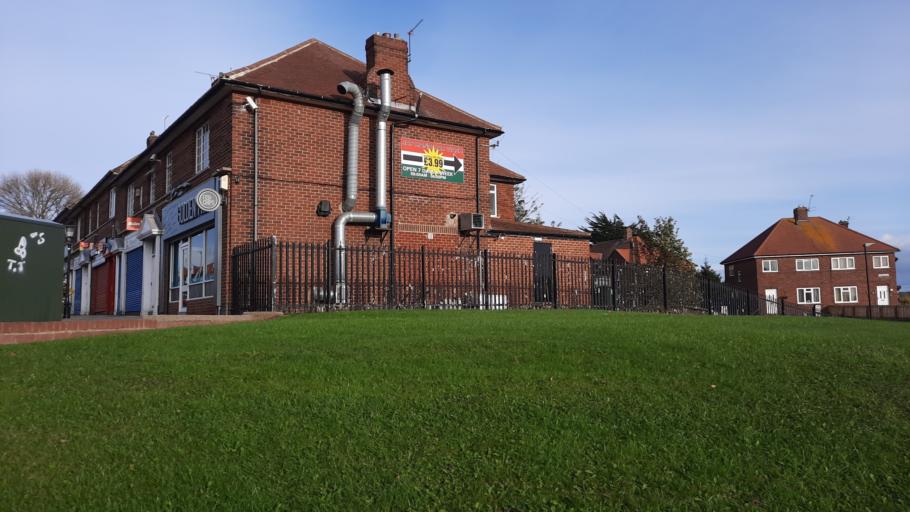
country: GB
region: England
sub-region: Sunderland
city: Sunderland
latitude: 54.8880
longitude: -1.4182
